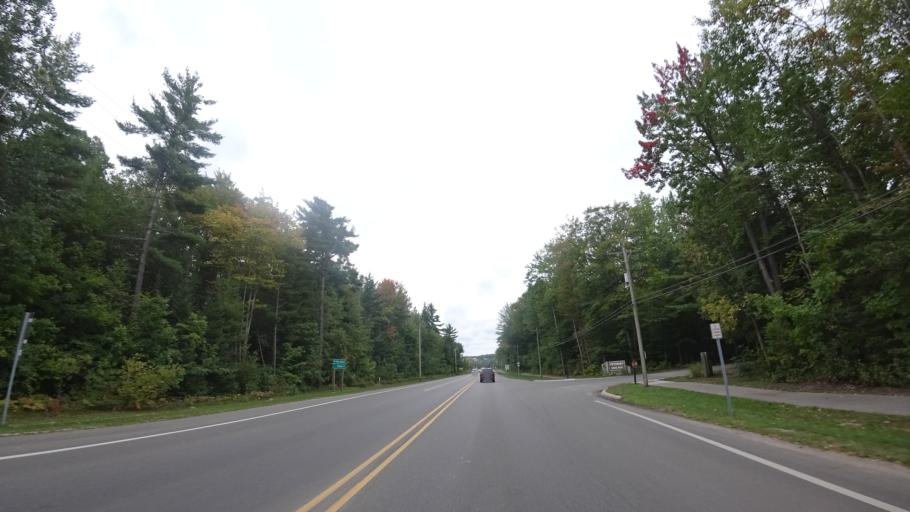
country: US
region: Michigan
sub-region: Emmet County
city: Petoskey
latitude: 45.4085
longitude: -84.9021
